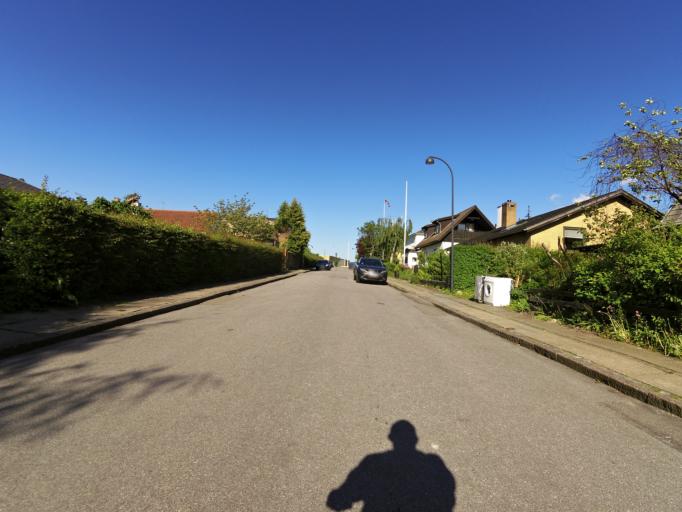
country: DK
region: Capital Region
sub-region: Lyngby-Tarbaek Kommune
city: Kongens Lyngby
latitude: 55.7362
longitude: 12.5388
